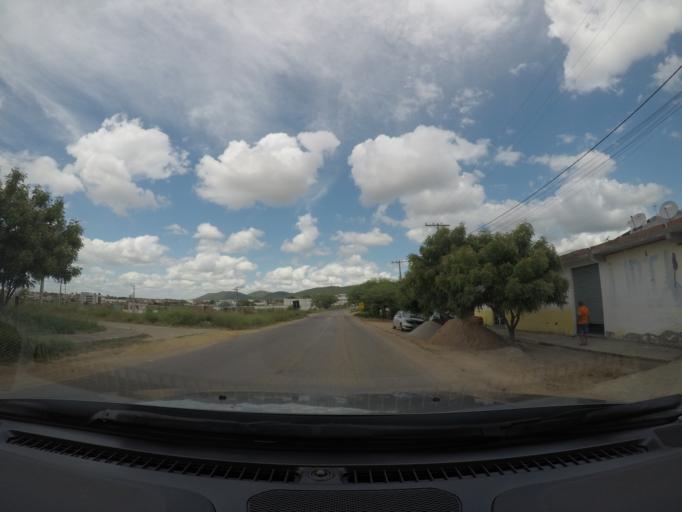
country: BR
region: Bahia
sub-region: Ipira
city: Ipira
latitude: -12.1646
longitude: -39.7482
